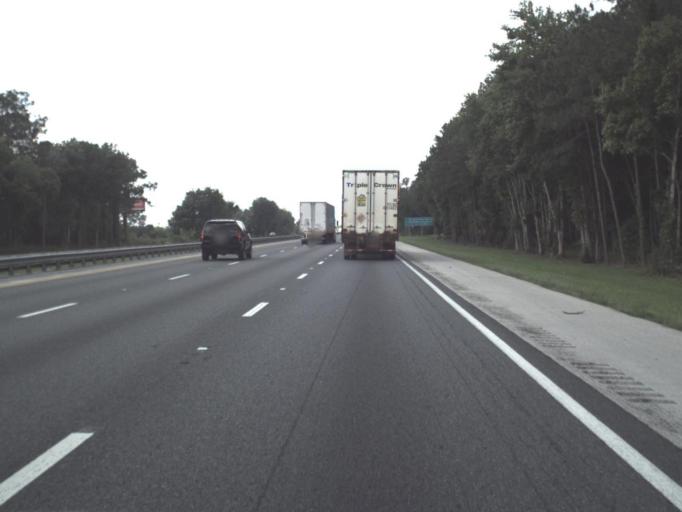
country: US
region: Florida
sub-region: Saint Johns County
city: Saint Augustine
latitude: 29.9028
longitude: -81.4074
